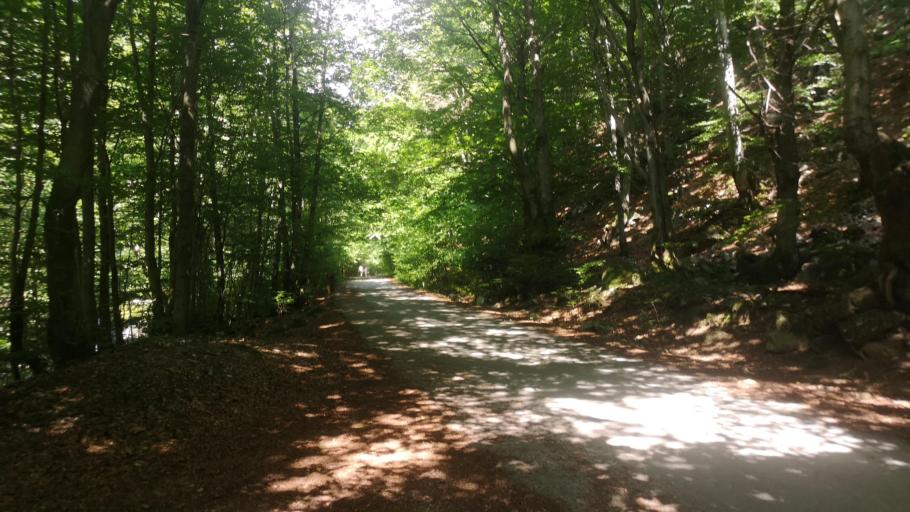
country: SK
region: Zilinsky
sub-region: Okres Zilina
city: Terchova
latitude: 49.1629
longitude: 19.0838
